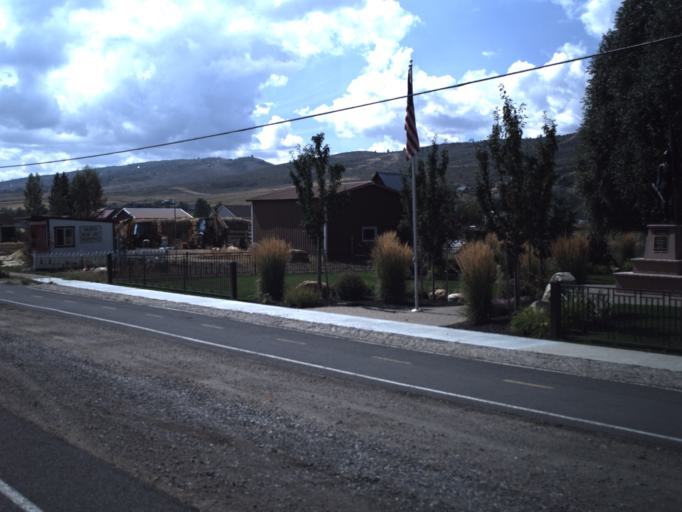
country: US
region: Idaho
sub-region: Bear Lake County
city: Paris
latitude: 41.9395
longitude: -111.3936
